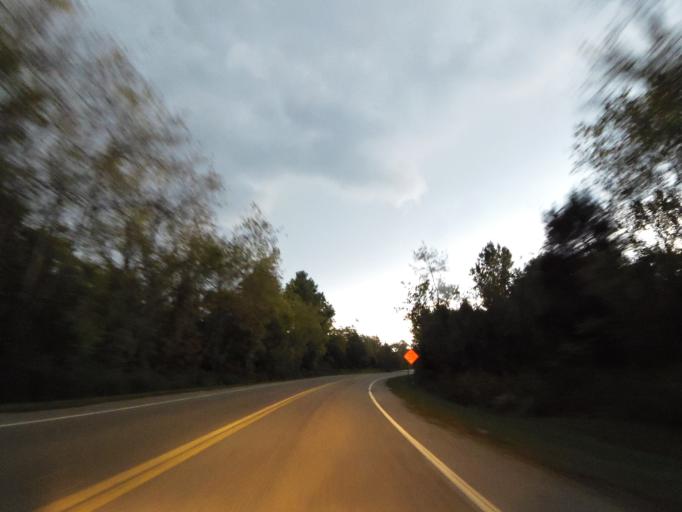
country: US
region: Tennessee
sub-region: Loudon County
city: Lenoir City
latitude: 35.7835
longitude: -84.2489
